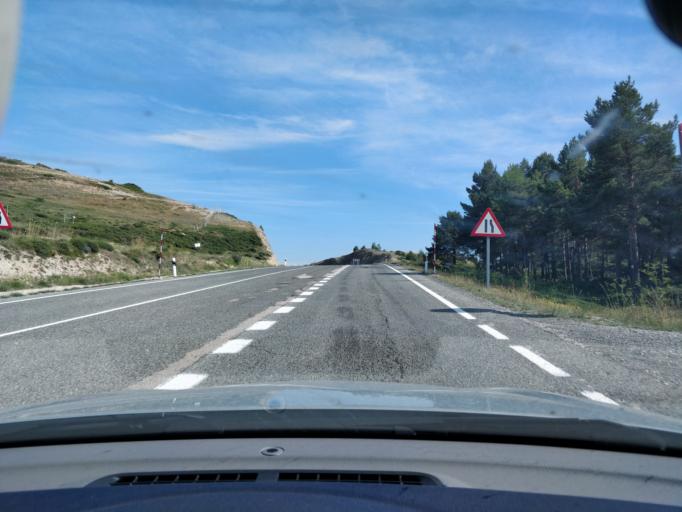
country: ES
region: Castille and Leon
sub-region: Provincia de Burgos
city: Espinosa de los Monteros
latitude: 42.9395
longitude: -3.6720
